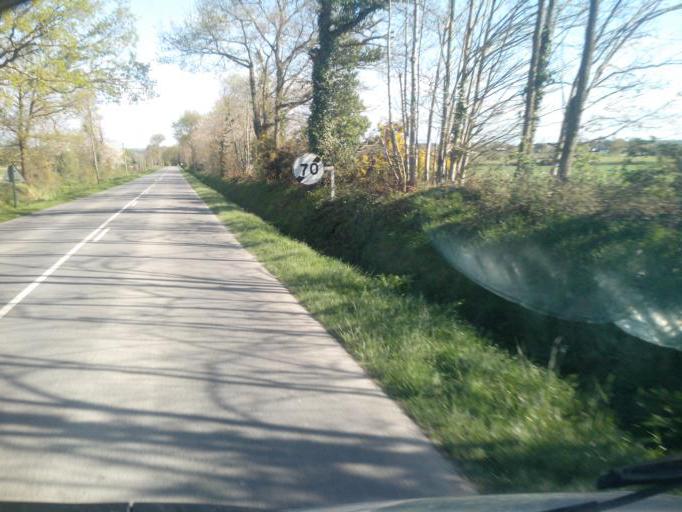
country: FR
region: Brittany
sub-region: Departement d'Ille-et-Vilaine
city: Guipry
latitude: 47.8509
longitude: -1.8736
